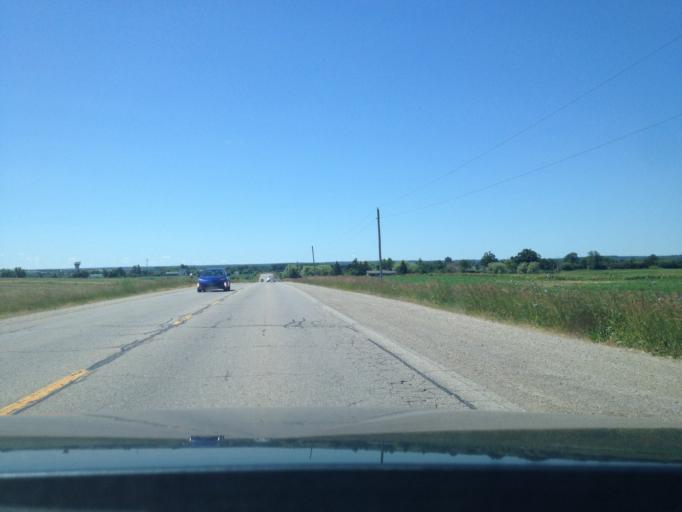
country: CA
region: Ontario
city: Brampton
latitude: 43.6739
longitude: -79.8901
